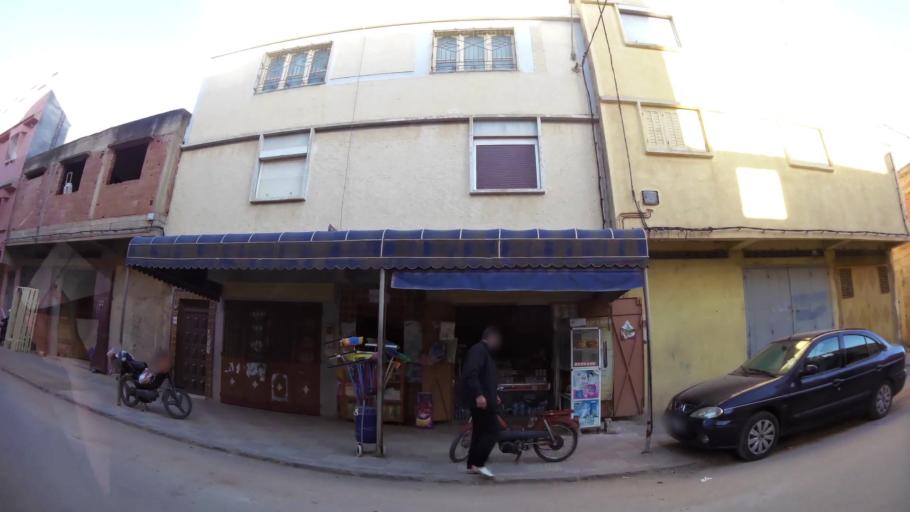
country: MA
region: Oriental
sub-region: Berkane-Taourirt
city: Berkane
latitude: 34.9303
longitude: -2.3260
